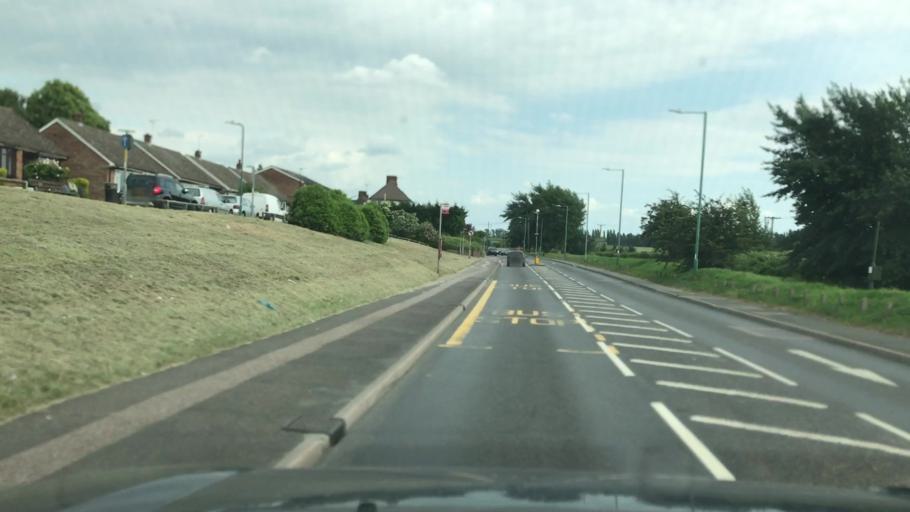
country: GB
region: England
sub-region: Kent
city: Stone
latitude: 51.4205
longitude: 0.2529
